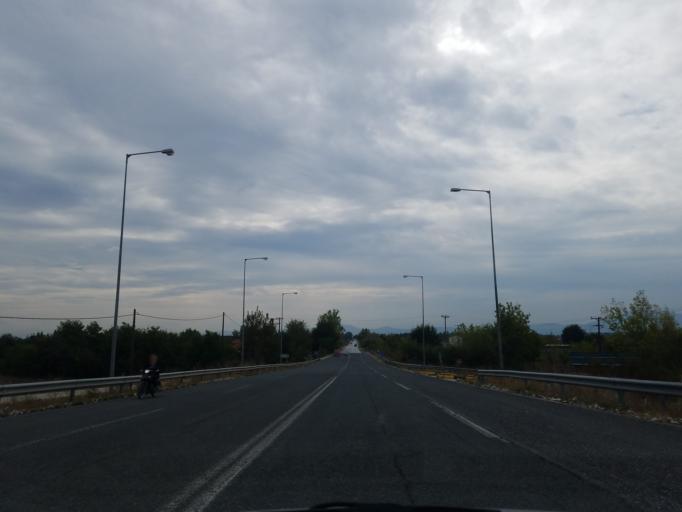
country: GR
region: Thessaly
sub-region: Nomos Kardhitsas
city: Sofades
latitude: 39.3400
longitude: 22.0825
